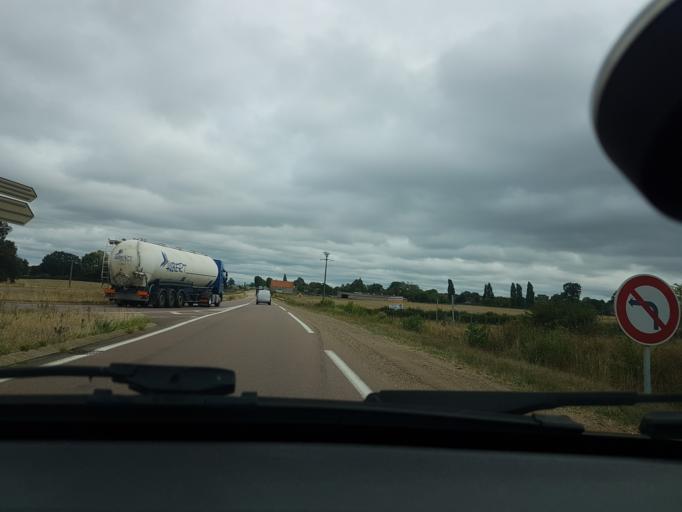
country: FR
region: Bourgogne
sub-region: Departement de l'Yonne
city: Avallon
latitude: 47.4860
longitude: 3.9903
